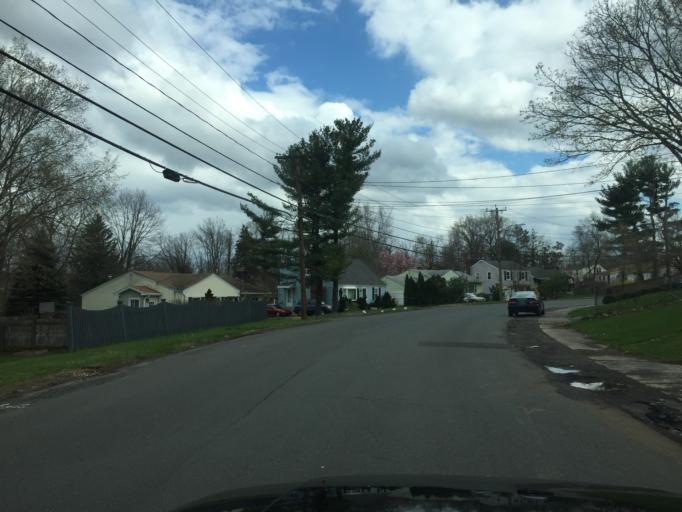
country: US
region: Connecticut
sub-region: Hartford County
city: New Britain
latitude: 41.7017
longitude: -72.7927
